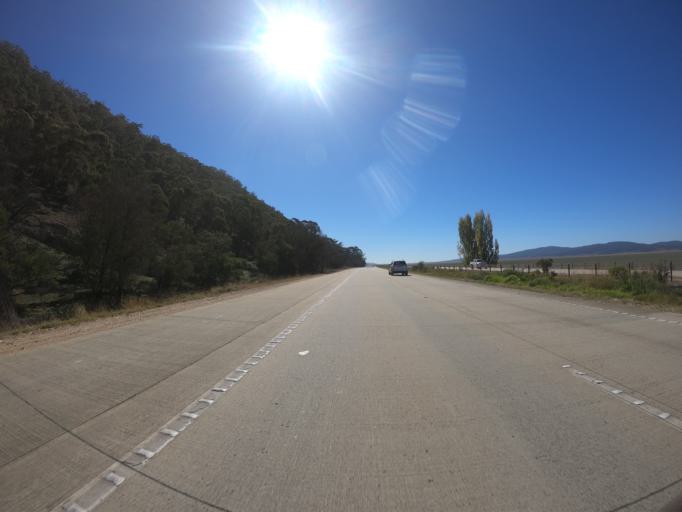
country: AU
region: New South Wales
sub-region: Yass Valley
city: Gundaroo
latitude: -35.0487
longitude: 149.3758
